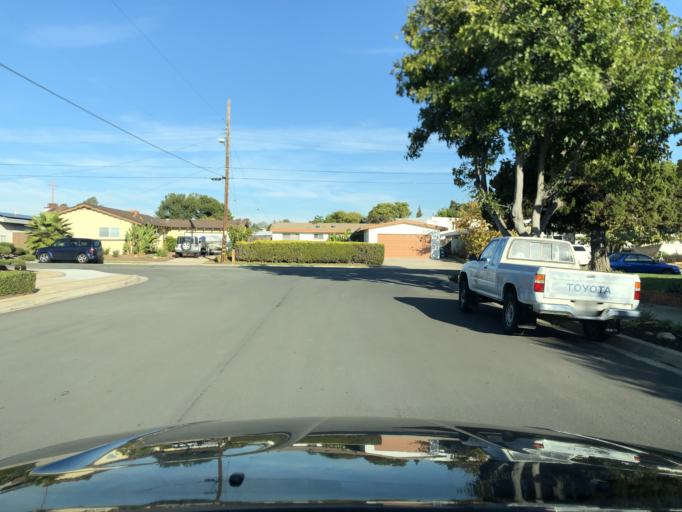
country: US
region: California
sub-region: San Diego County
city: La Jolla
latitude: 32.8258
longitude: -117.1927
